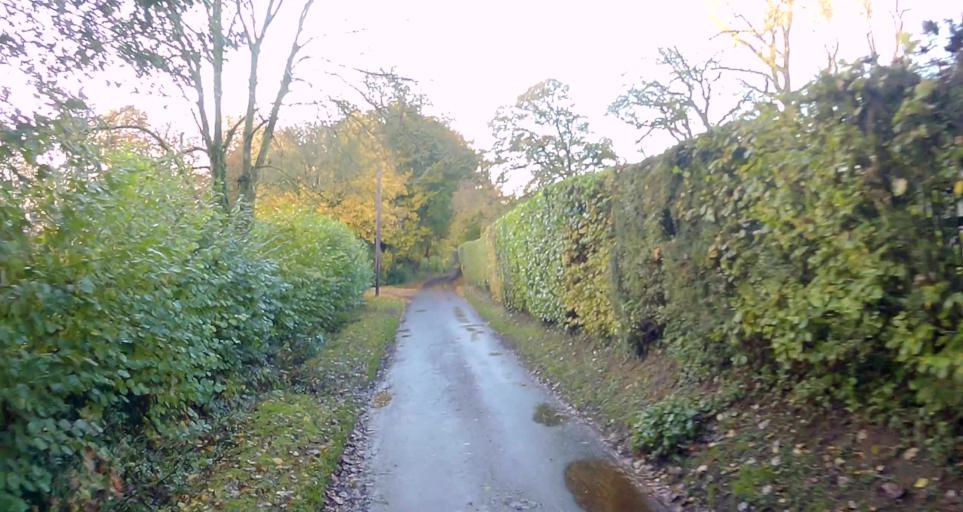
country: GB
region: England
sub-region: Hampshire
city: Basingstoke
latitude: 51.2069
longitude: -1.0803
